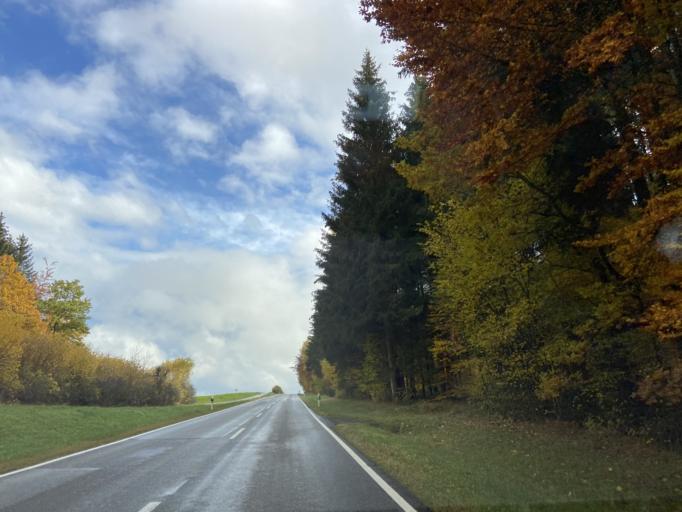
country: DE
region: Baden-Wuerttemberg
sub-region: Tuebingen Region
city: Messkirch
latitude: 48.0525
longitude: 9.0892
